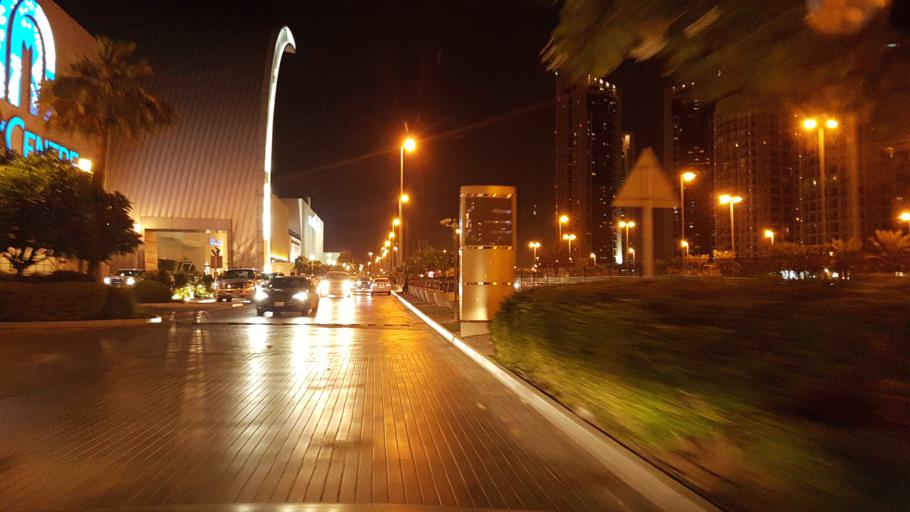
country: BH
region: Manama
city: Jidd Hafs
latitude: 26.2324
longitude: 50.5529
